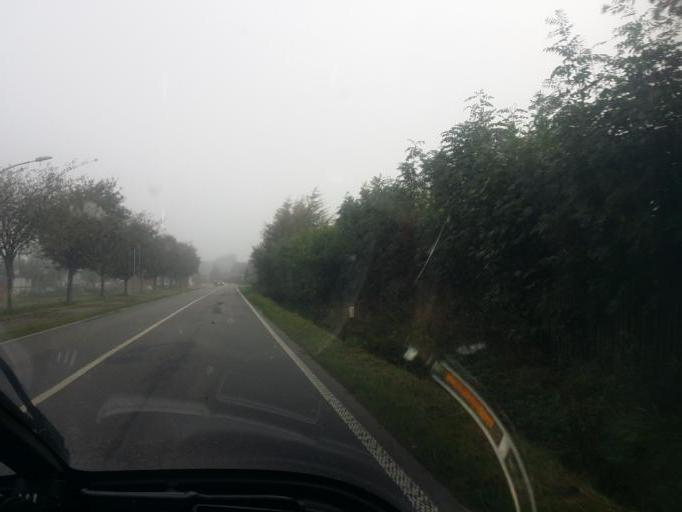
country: DE
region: Schleswig-Holstein
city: Horstedt
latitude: 54.5222
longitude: 9.0675
